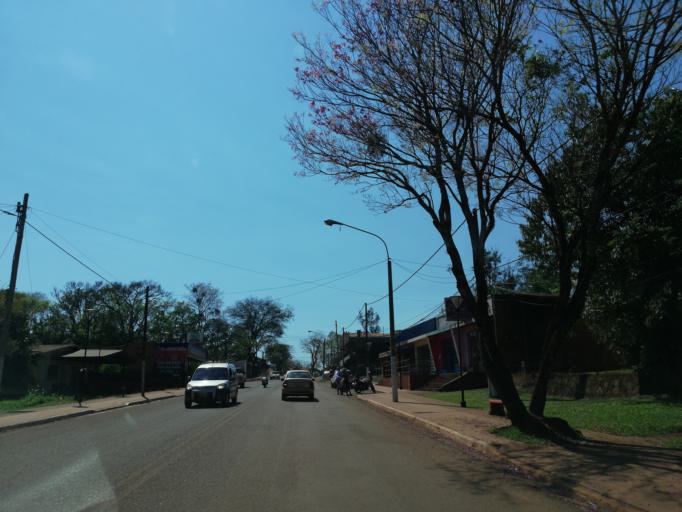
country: AR
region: Misiones
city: Puerto Eldorado
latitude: -26.4077
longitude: -54.6696
